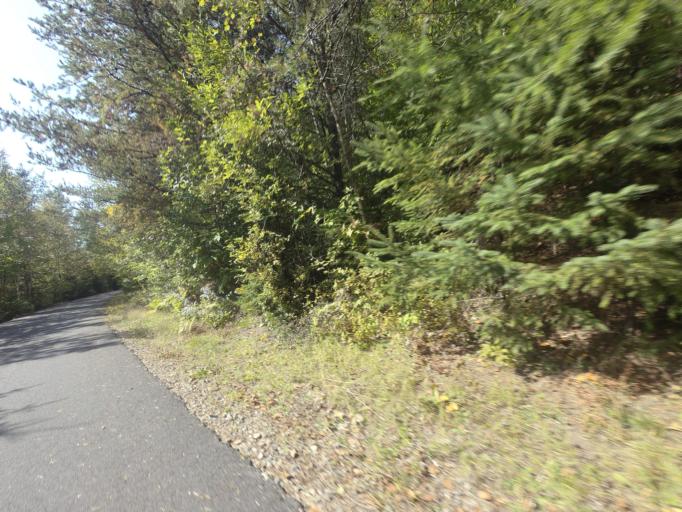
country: CA
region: Quebec
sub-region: Laurentides
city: Mont-Tremblant
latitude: 46.1123
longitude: -74.5114
